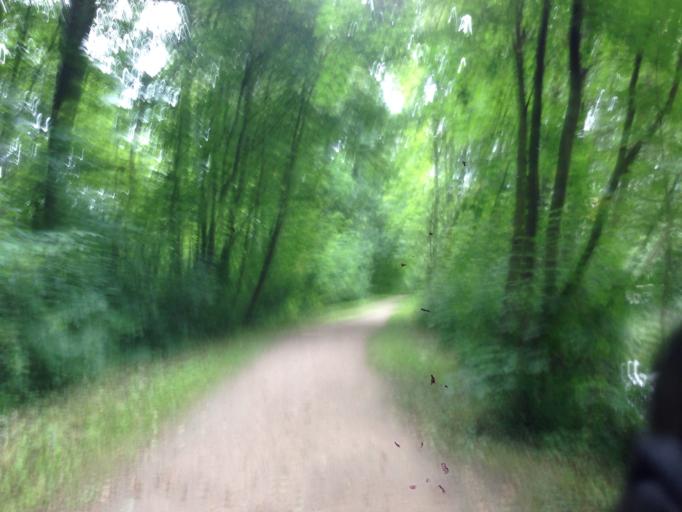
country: DE
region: Hamburg
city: Farmsen-Berne
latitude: 53.5941
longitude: 10.1188
